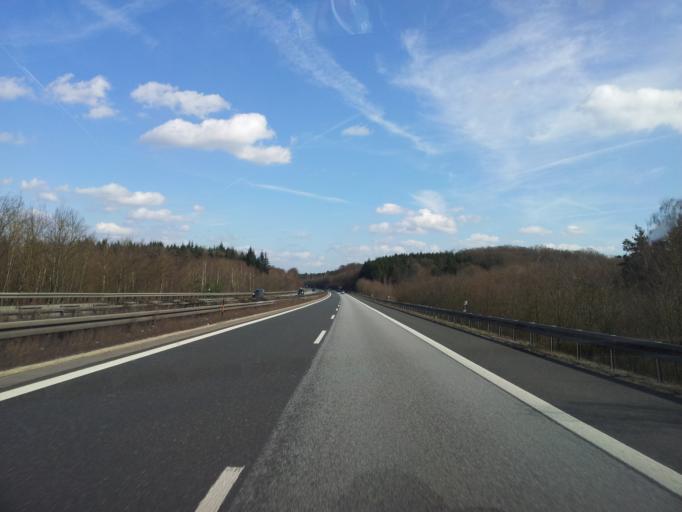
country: DE
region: Bavaria
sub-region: Regierungsbezirk Unterfranken
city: Donnersdorf
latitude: 50.0048
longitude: 10.3917
